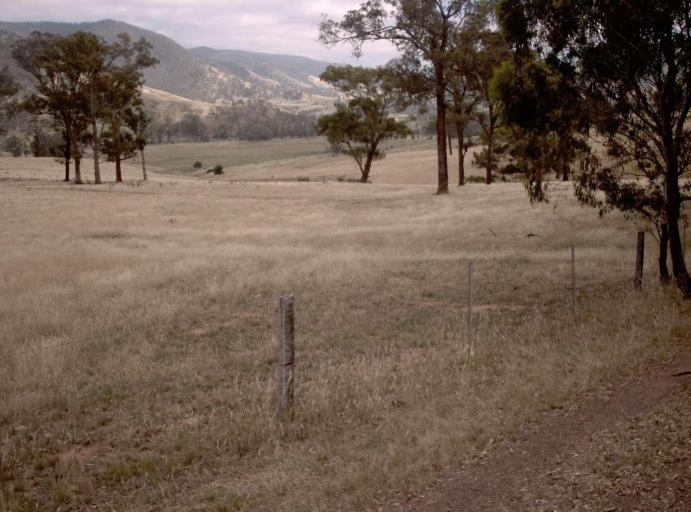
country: AU
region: Victoria
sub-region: Wellington
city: Heyfield
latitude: -37.6560
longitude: 146.6423
